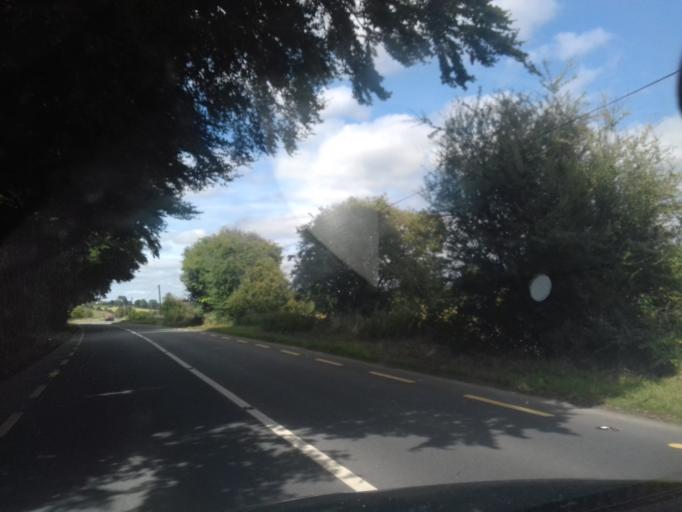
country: IE
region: Leinster
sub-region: Wicklow
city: Valleymount
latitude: 53.0392
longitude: -6.6356
